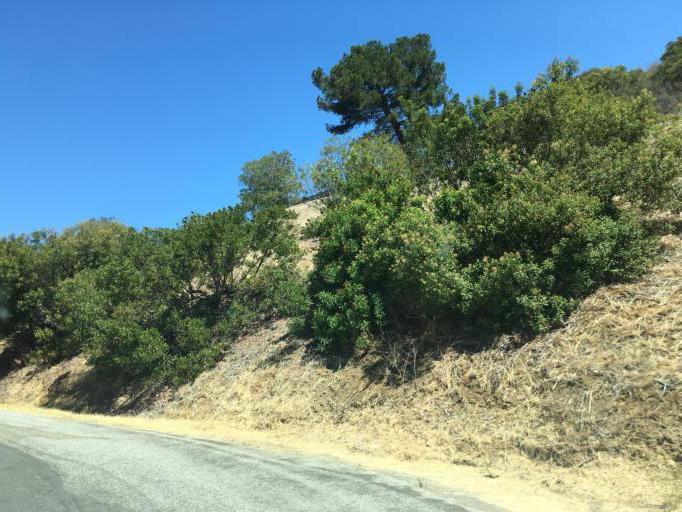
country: US
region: California
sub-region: Los Angeles County
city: Malibu Beach
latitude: 34.0463
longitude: -118.7408
